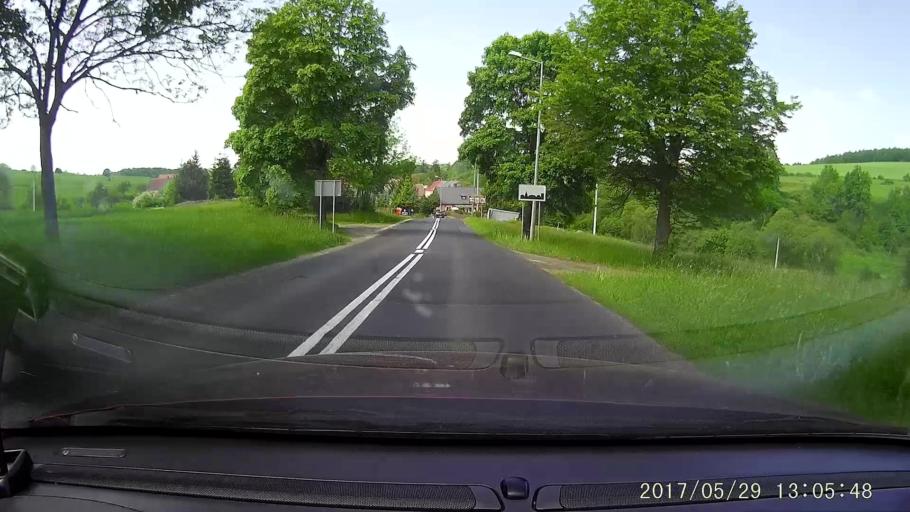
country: PL
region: Lower Silesian Voivodeship
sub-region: Powiat jeleniogorski
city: Stara Kamienica
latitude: 50.9473
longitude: 15.5870
